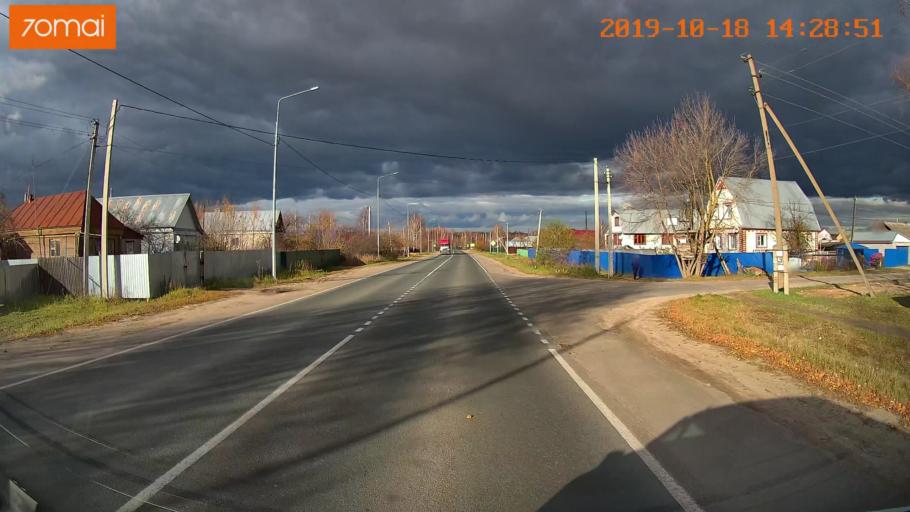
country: RU
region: Rjazan
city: Tuma
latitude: 55.1516
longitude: 40.5549
